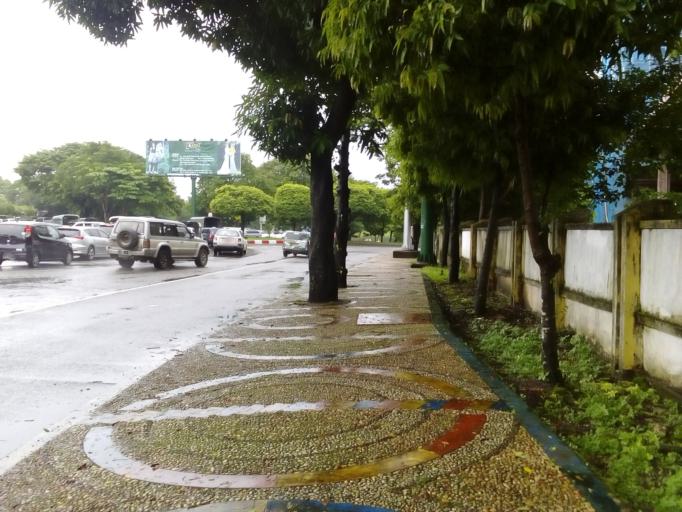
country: MM
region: Yangon
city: Yangon
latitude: 16.7946
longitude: 96.1464
